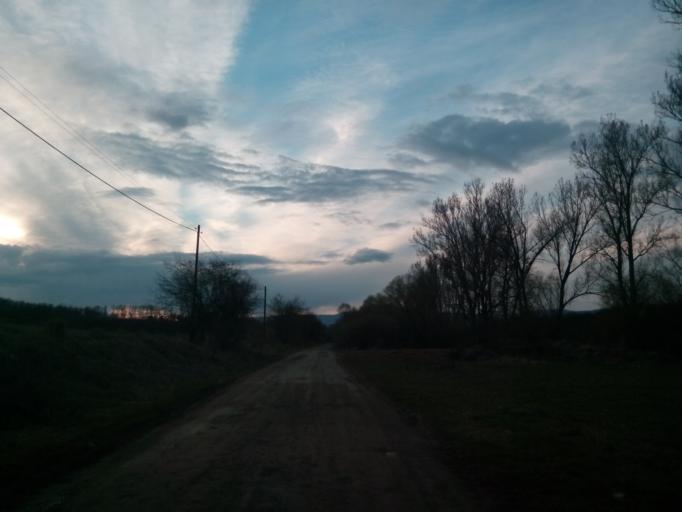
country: SK
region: Kosicky
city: Moldava nad Bodvou
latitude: 48.5491
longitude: 20.9794
